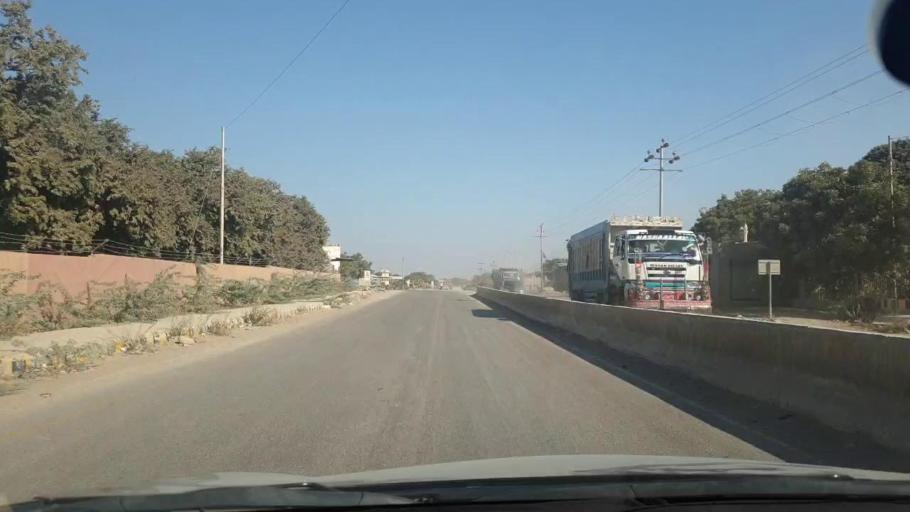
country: PK
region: Sindh
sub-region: Karachi District
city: Karachi
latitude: 25.0900
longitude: 67.0131
